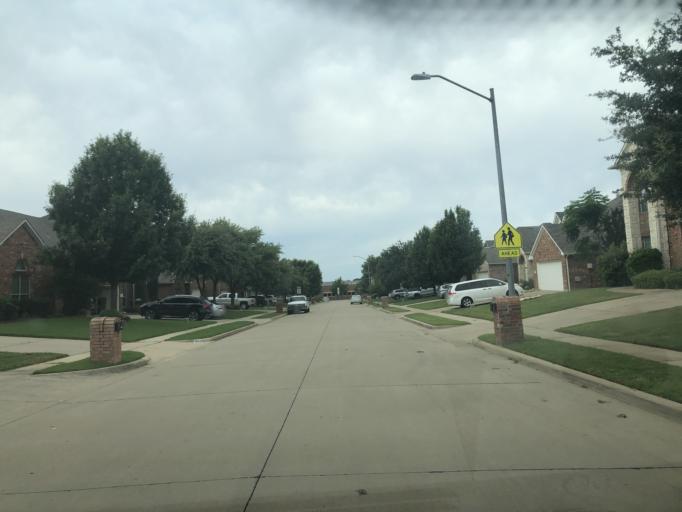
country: US
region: Texas
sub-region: Dallas County
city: Irving
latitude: 32.7984
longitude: -96.9869
